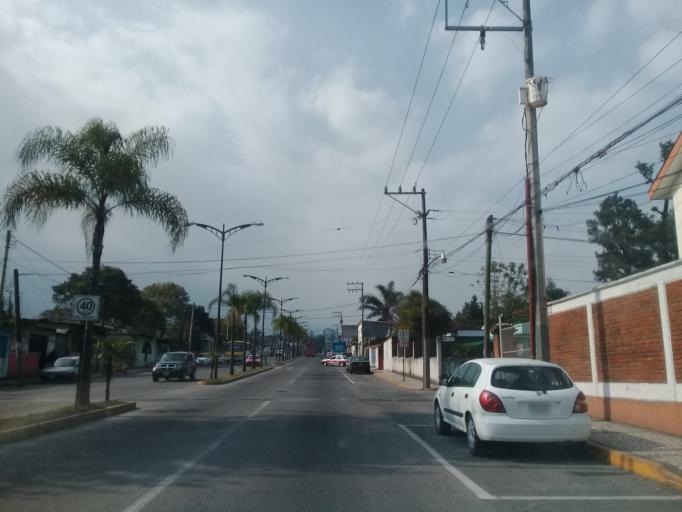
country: MX
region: Veracruz
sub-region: Ixhuatlancillo
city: Union y Progreso
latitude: 18.8666
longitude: -97.1122
